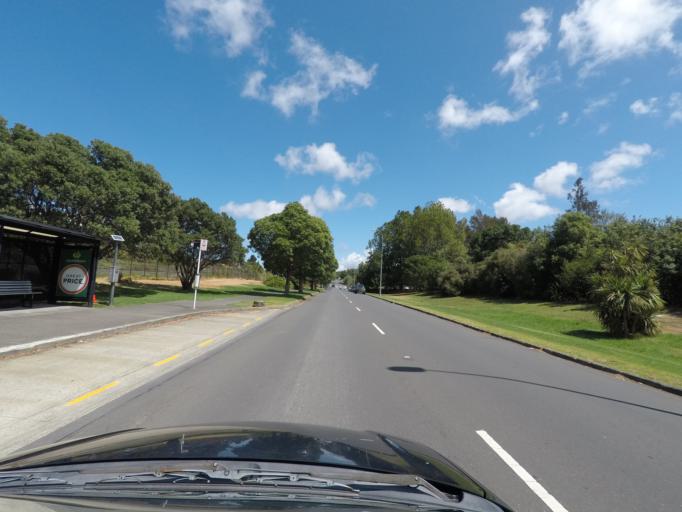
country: NZ
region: Auckland
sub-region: Auckland
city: Rosebank
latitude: -36.8595
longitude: 174.7141
